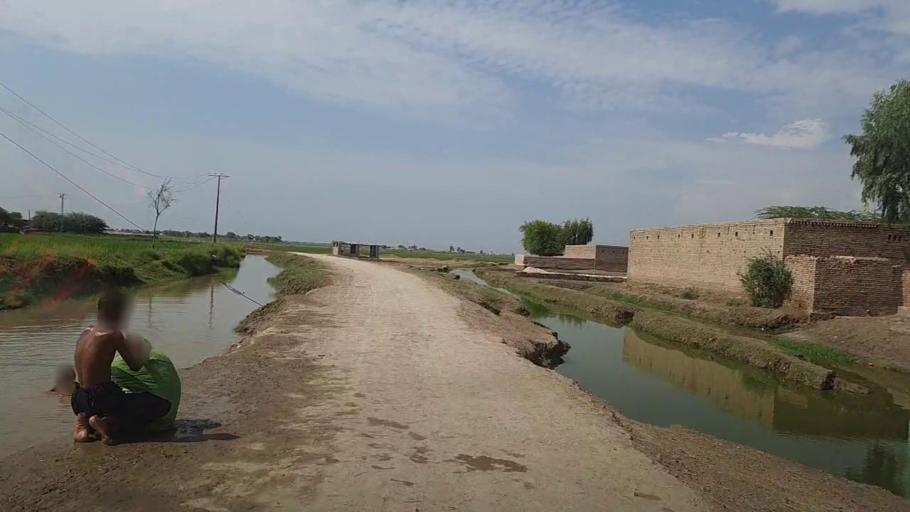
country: PK
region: Sindh
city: Thul
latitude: 28.2546
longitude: 68.8068
